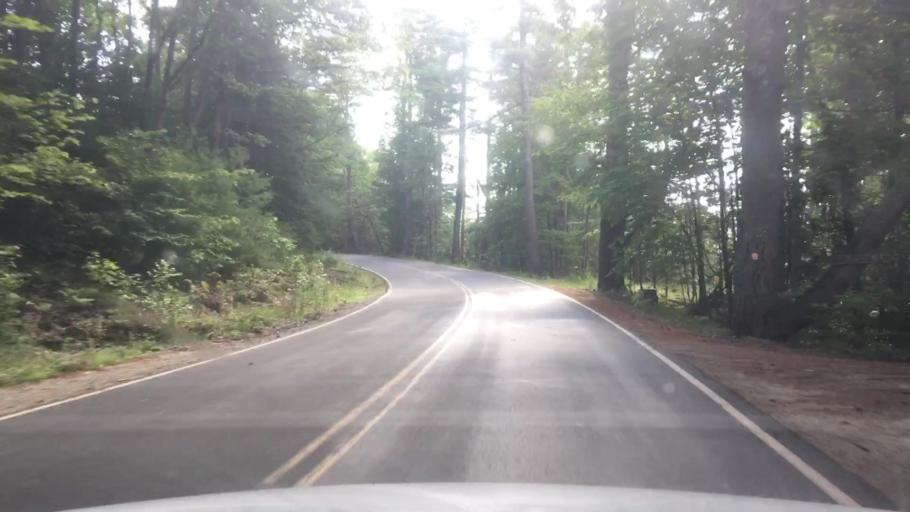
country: US
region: Maine
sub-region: Kennebec County
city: Gardiner
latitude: 44.1624
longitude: -69.8010
